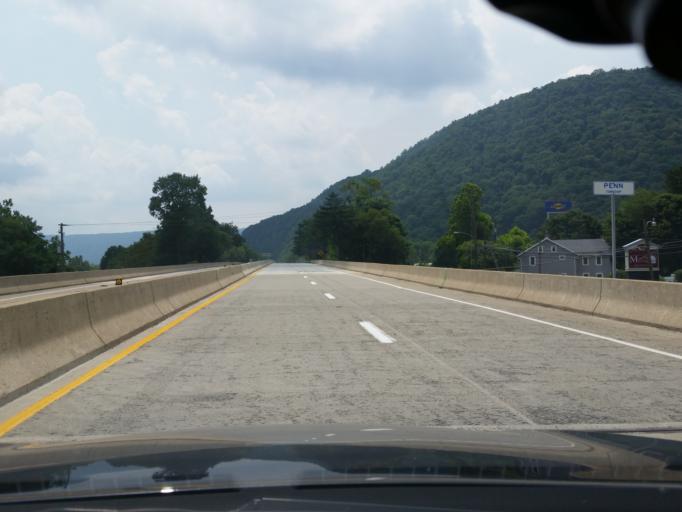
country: US
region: Pennsylvania
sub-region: Perry County
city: Duncannon
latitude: 40.3883
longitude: -77.0319
